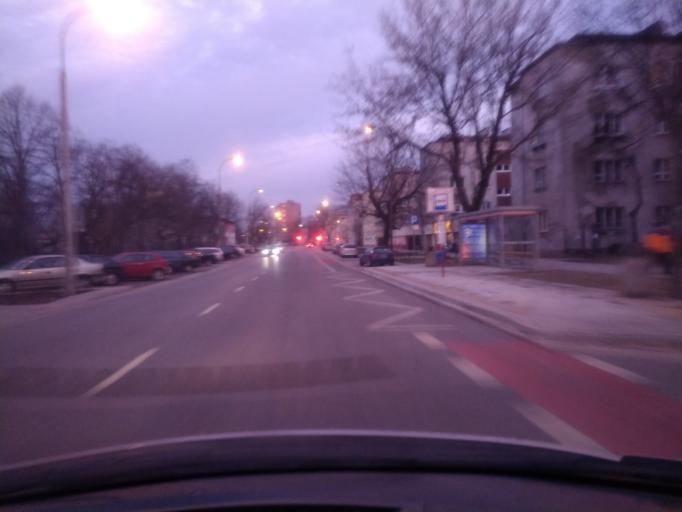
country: PL
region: Masovian Voivodeship
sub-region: Warszawa
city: Praga Poludnie
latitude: 52.2502
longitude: 21.0713
